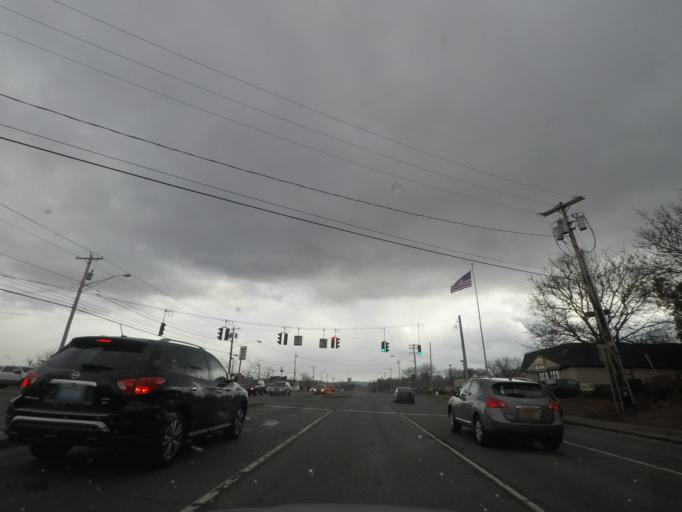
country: US
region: New York
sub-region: Onondaga County
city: East Syracuse
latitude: 43.0476
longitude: -76.0700
